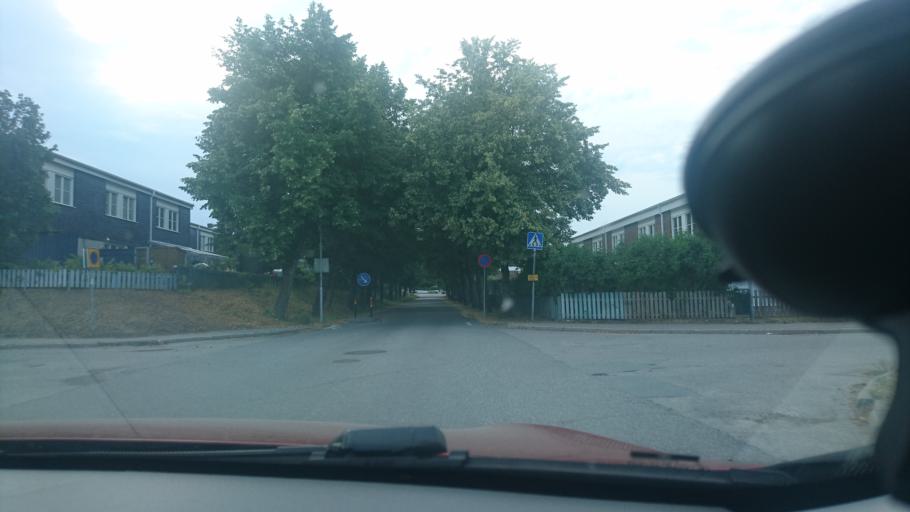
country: SE
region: Stockholm
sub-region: Upplands Vasby Kommun
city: Upplands Vaesby
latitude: 59.5076
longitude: 17.9179
